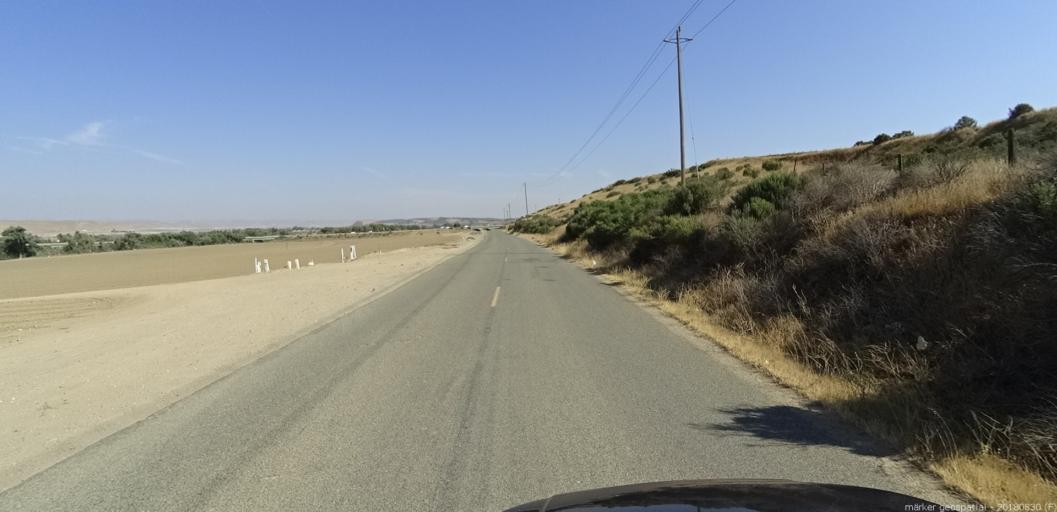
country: US
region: California
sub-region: Monterey County
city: King City
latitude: 36.1077
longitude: -121.0297
